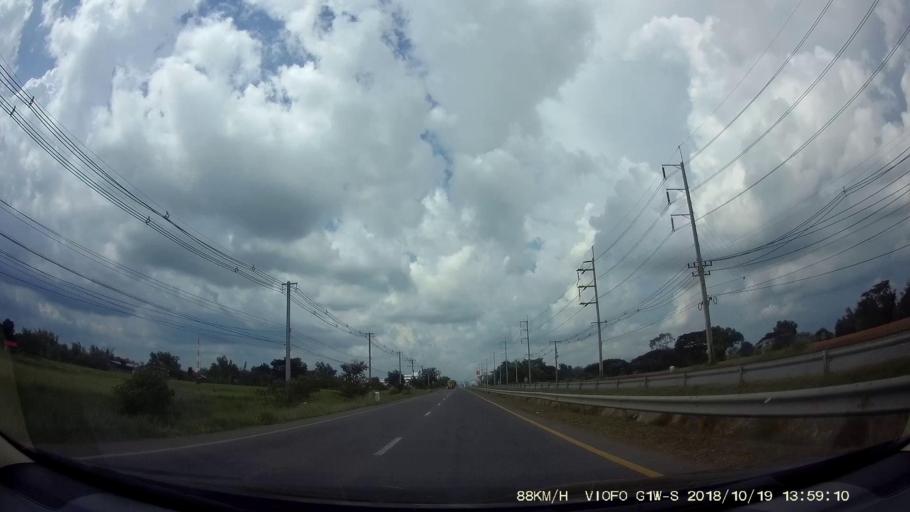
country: TH
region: Chaiyaphum
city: Chaiyaphum
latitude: 15.8058
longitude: 102.0612
